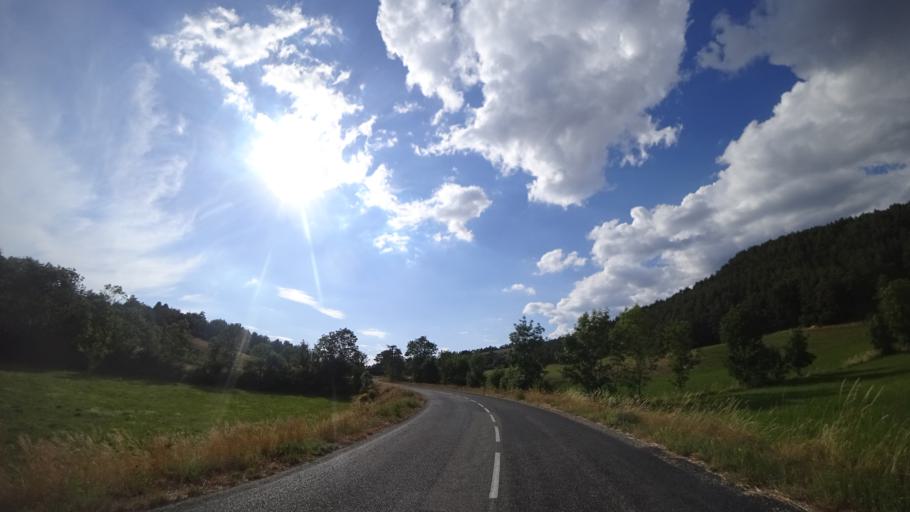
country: FR
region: Languedoc-Roussillon
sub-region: Departement de la Lozere
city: Chanac
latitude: 44.3753
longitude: 3.3313
